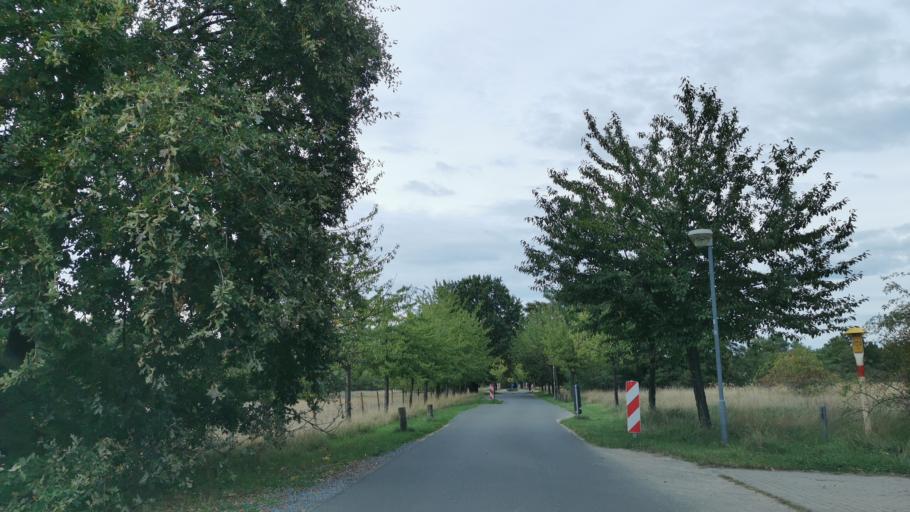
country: DE
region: Brandenburg
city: Werder
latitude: 52.3575
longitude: 12.9482
